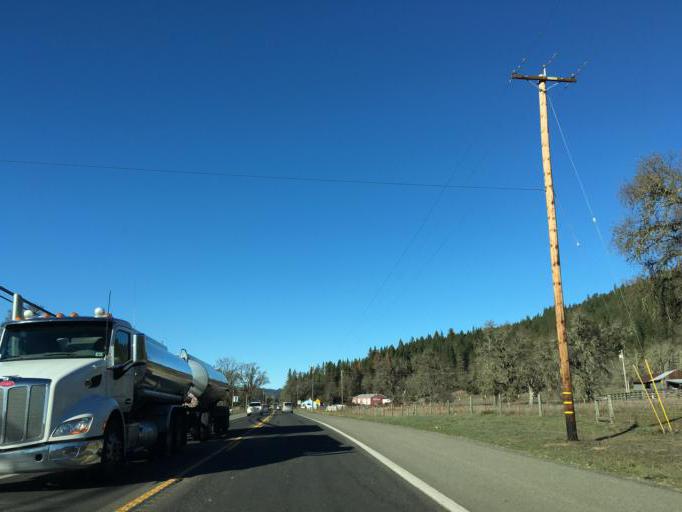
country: US
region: California
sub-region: Mendocino County
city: Laytonville
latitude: 39.6915
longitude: -123.4832
